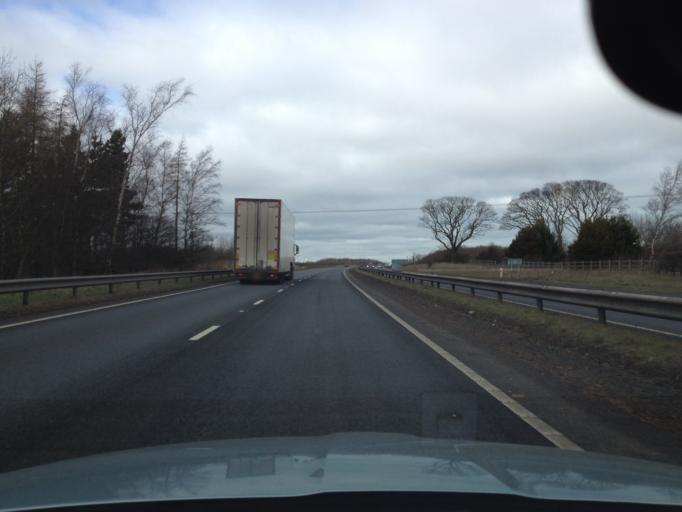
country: GB
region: Scotland
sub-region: East Lothian
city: Macmerry
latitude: 55.9477
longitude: -2.9123
